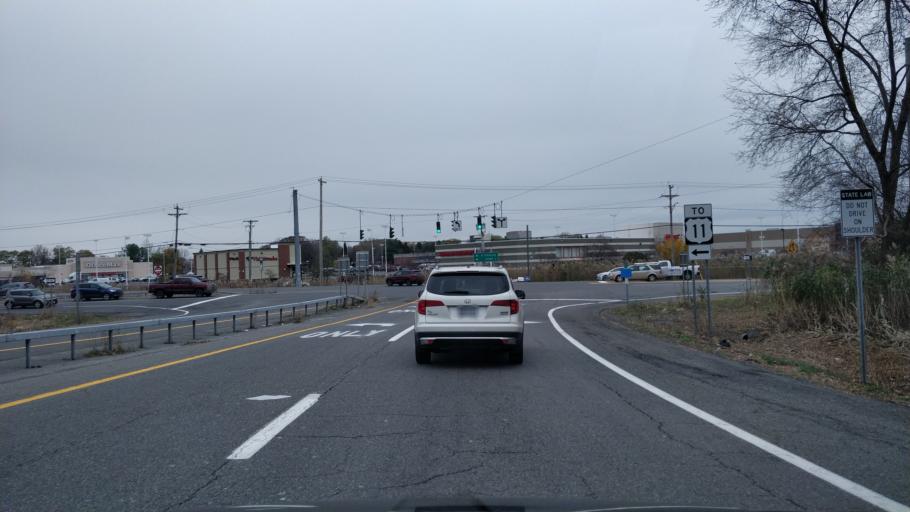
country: US
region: New York
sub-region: Onondaga County
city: North Syracuse
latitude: 43.1484
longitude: -76.1232
